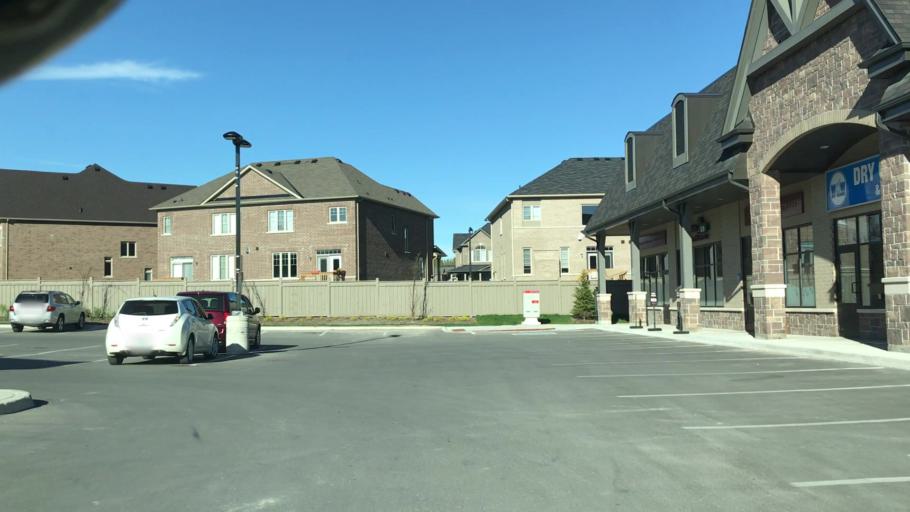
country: CA
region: Ontario
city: Newmarket
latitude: 44.0266
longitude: -79.4304
